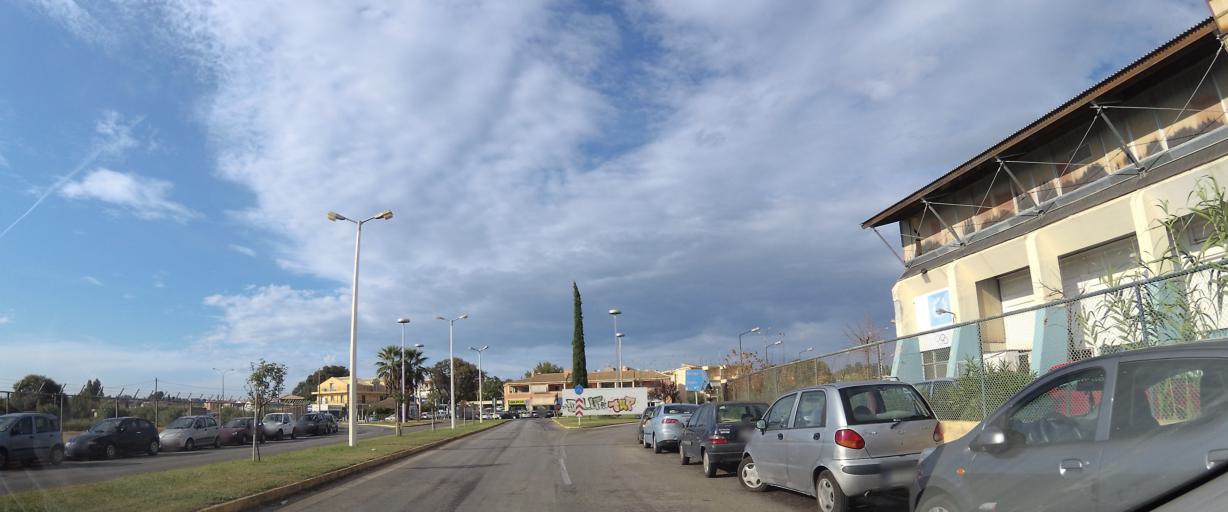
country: GR
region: Ionian Islands
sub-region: Nomos Kerkyras
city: Kerkyra
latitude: 39.6109
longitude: 19.9142
